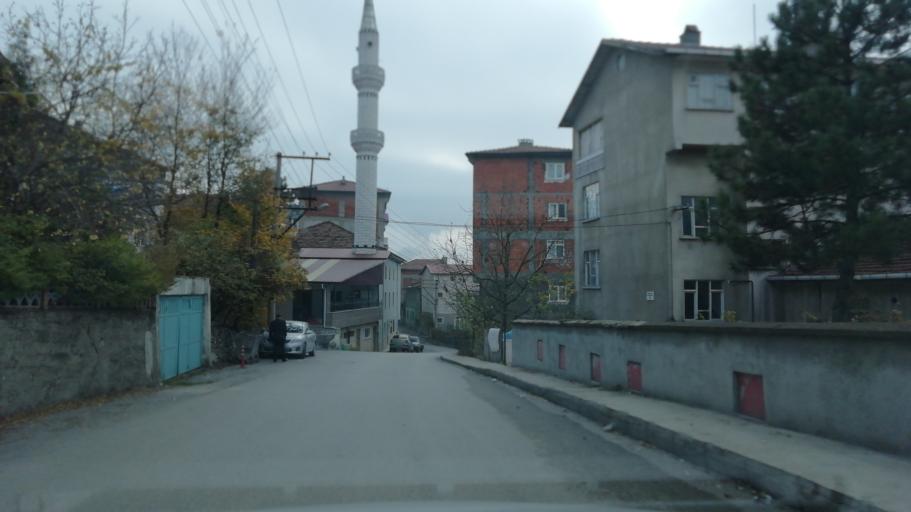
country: TR
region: Karabuk
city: Karabuk
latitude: 41.2161
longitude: 32.6287
